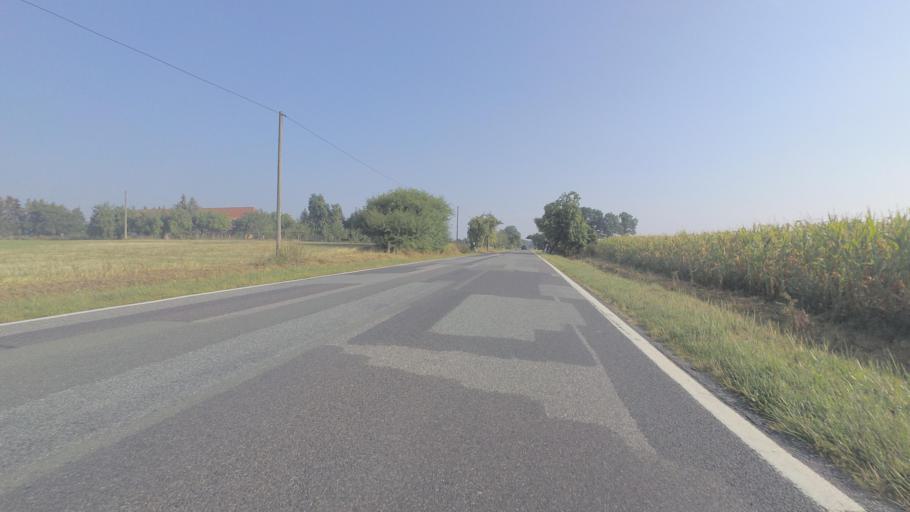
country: DE
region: Mecklenburg-Vorpommern
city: Malchow
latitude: 53.3679
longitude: 12.3841
